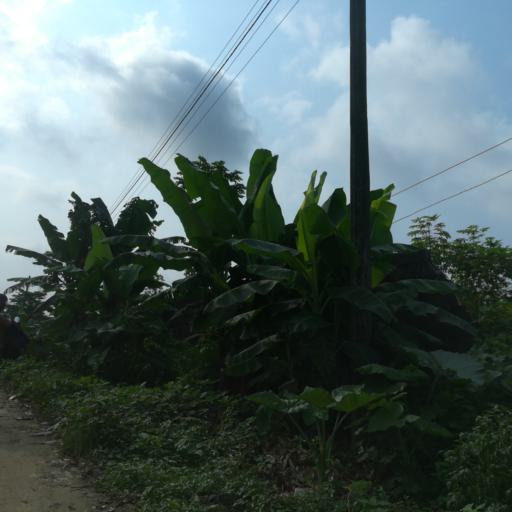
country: NG
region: Rivers
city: Okrika
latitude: 4.7831
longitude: 7.1392
